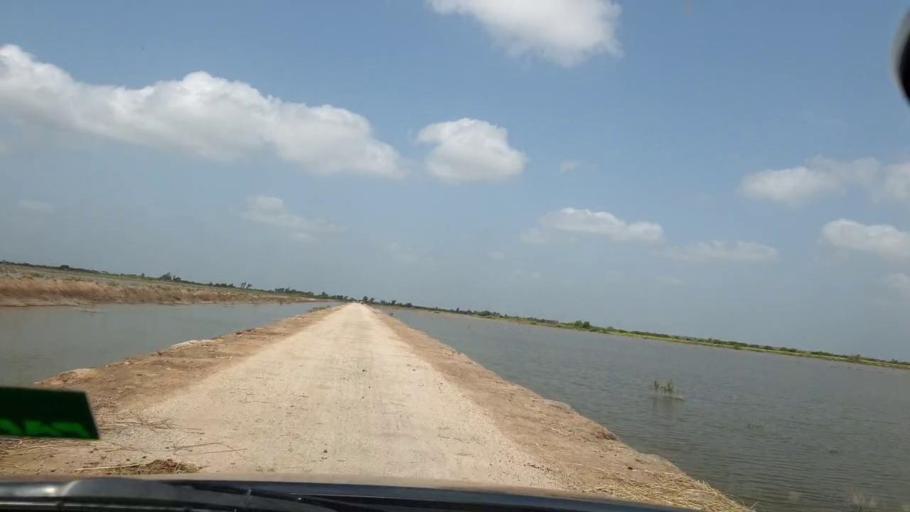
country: PK
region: Sindh
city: Kadhan
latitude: 24.5953
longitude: 69.1307
